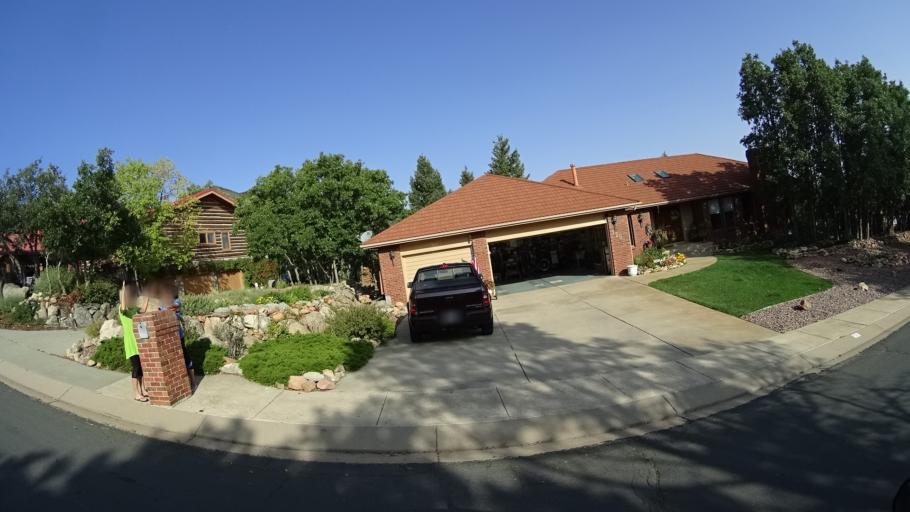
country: US
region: Colorado
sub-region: El Paso County
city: Manitou Springs
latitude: 38.8216
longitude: -104.8776
